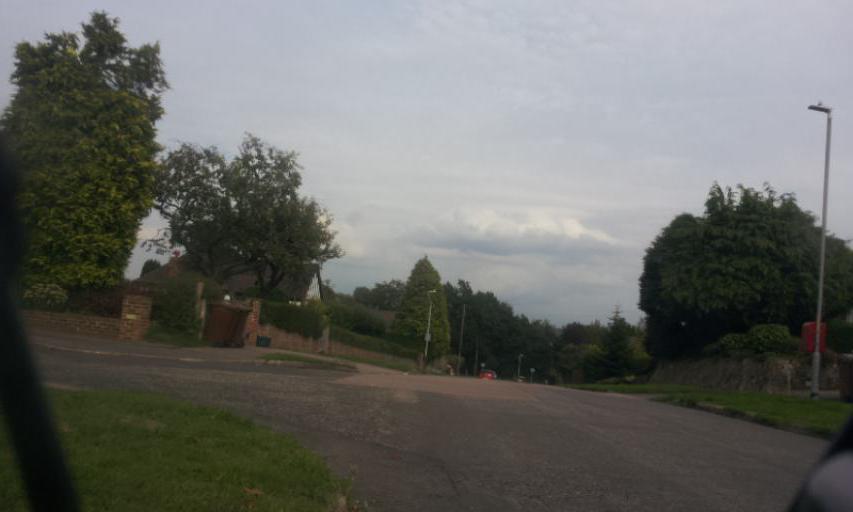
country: GB
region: England
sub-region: Kent
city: Tonbridge
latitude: 51.1697
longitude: 0.2504
